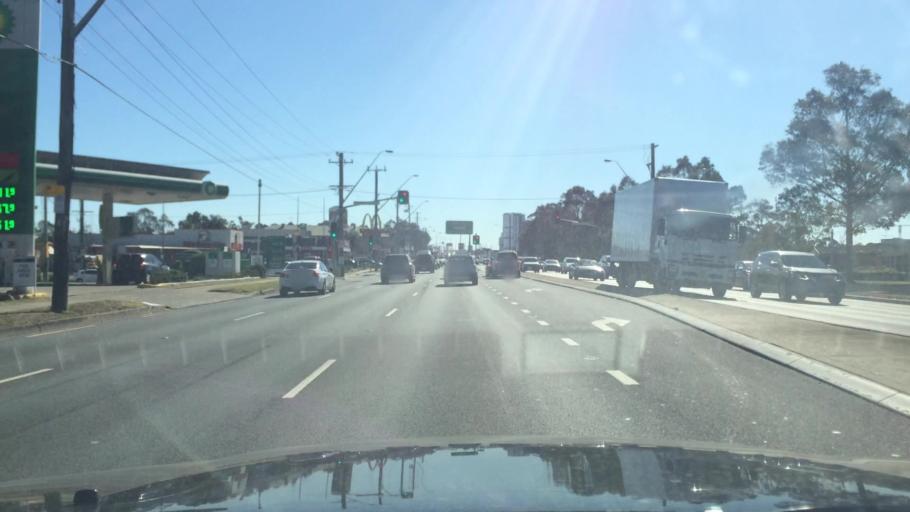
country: AU
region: New South Wales
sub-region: Campbelltown Municipality
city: Glenfield
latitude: -33.9414
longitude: 150.9121
